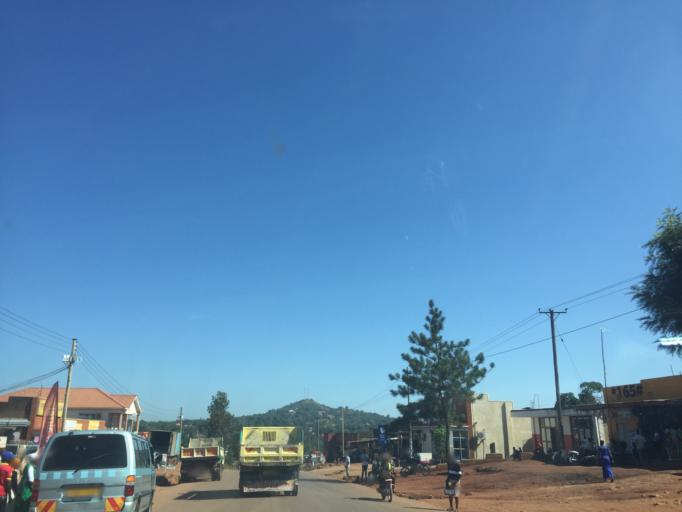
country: UG
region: Central Region
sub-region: Luwero District
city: Wobulenzi
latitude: 0.7194
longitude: 32.5282
